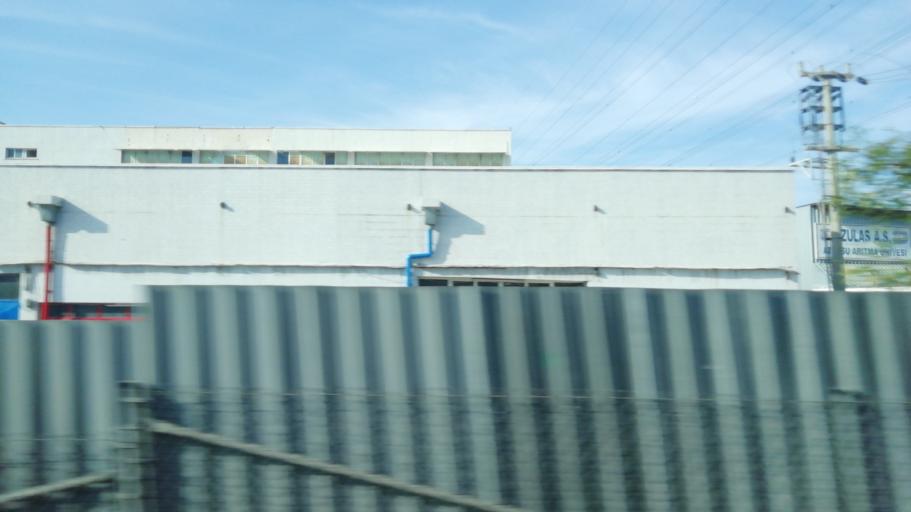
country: TR
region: Izmir
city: Bornova
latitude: 38.4591
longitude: 27.2436
